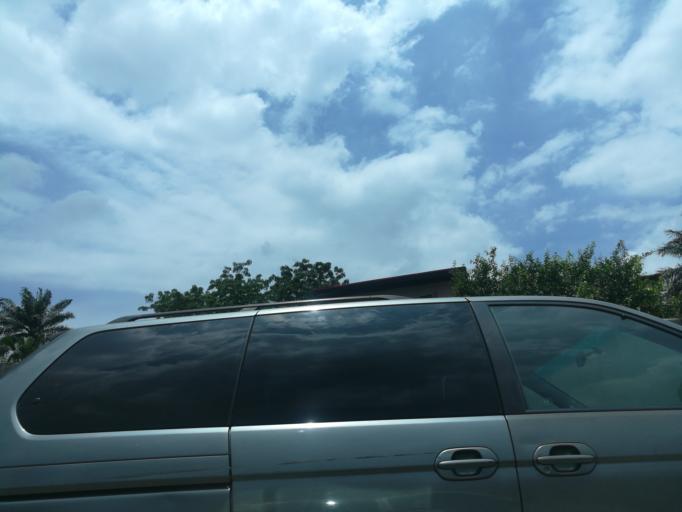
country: NG
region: Lagos
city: Somolu
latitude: 6.5507
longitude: 3.3656
